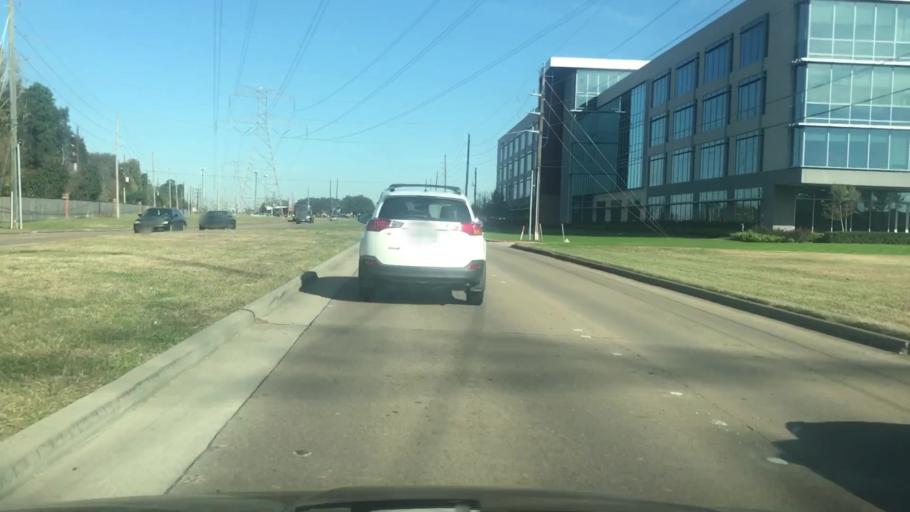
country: US
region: Texas
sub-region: Fort Bend County
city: Cinco Ranch
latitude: 29.7946
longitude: -95.7519
